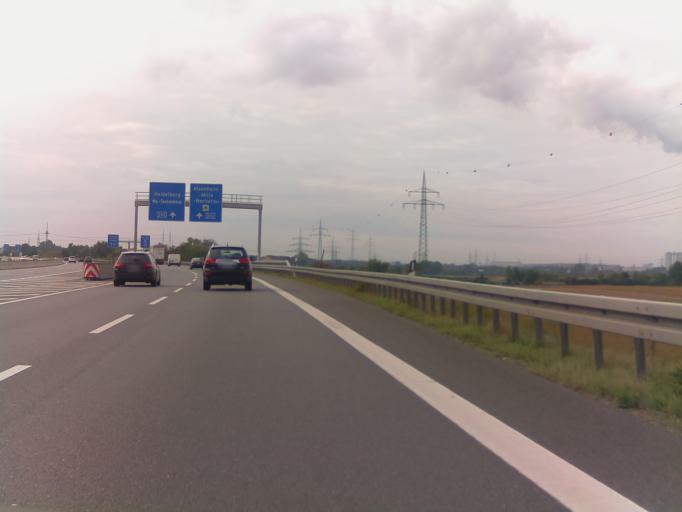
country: DE
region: Baden-Wuerttemberg
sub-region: Karlsruhe Region
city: Ilvesheim
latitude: 49.4675
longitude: 8.5400
